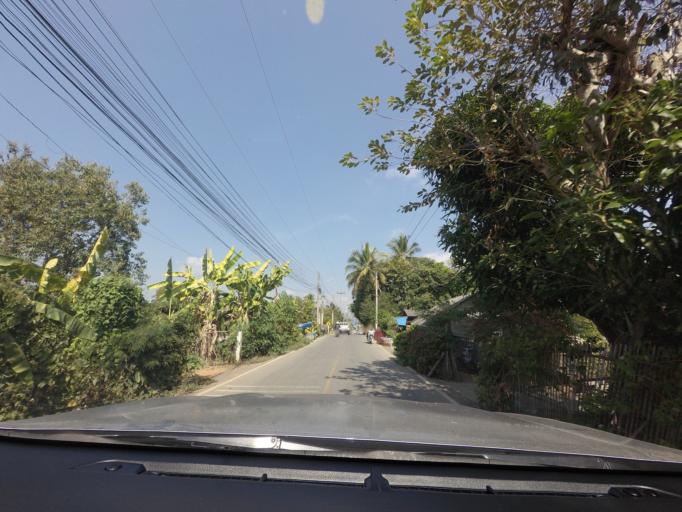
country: TH
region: Mae Hong Son
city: Wiang Nuea
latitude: 19.3762
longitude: 98.4455
